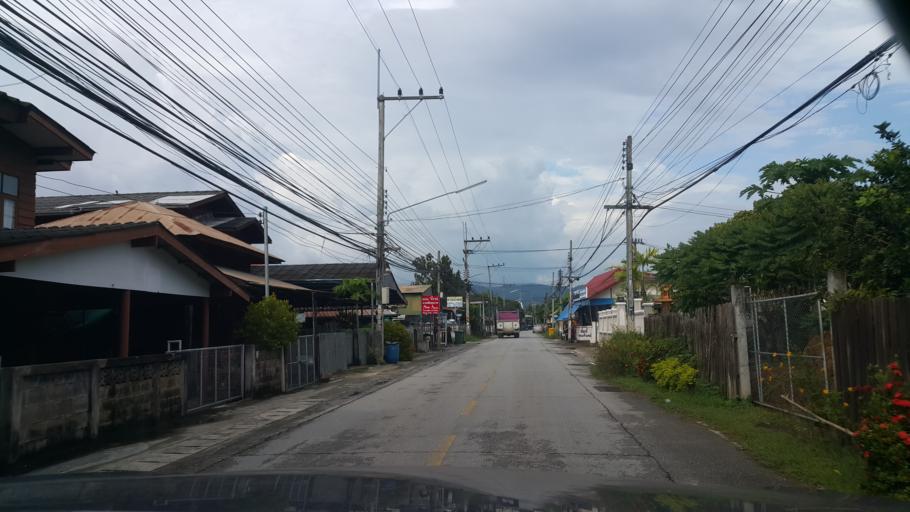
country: TH
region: Lampang
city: Thoen
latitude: 17.6187
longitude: 99.2227
